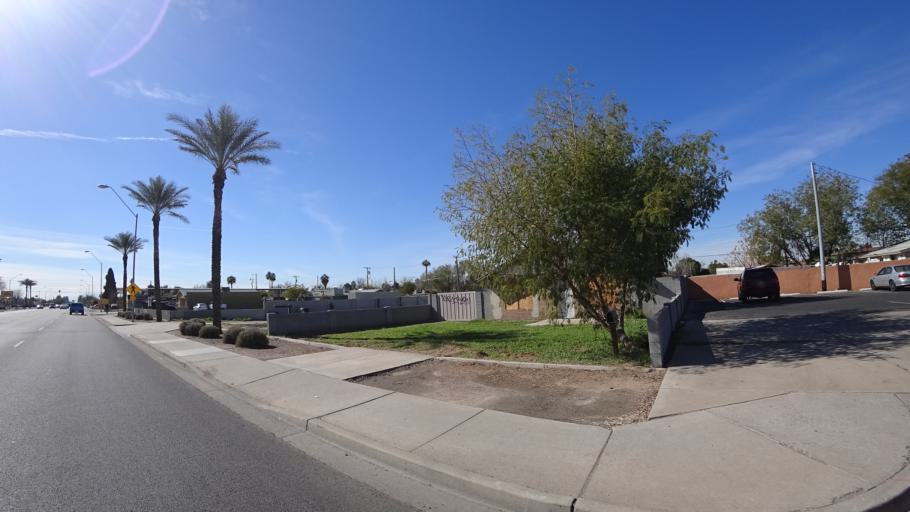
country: US
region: Arizona
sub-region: Maricopa County
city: Glendale
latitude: 33.5365
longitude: -112.1863
